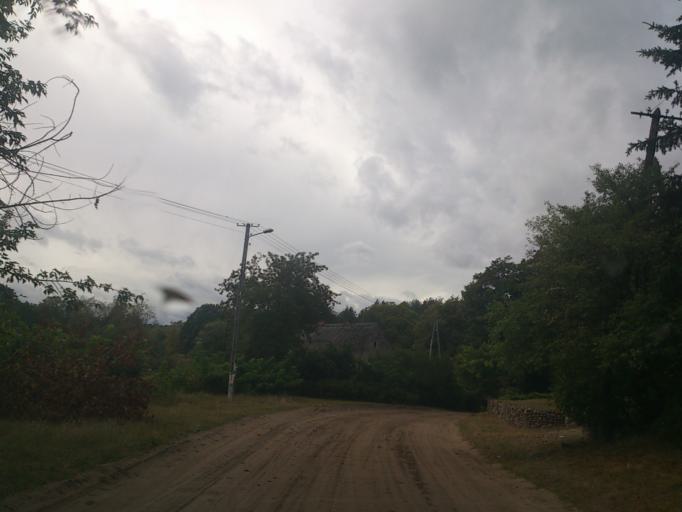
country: PL
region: Greater Poland Voivodeship
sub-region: Powiat poznanski
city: Murowana Goslina
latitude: 52.5543
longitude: 17.1123
